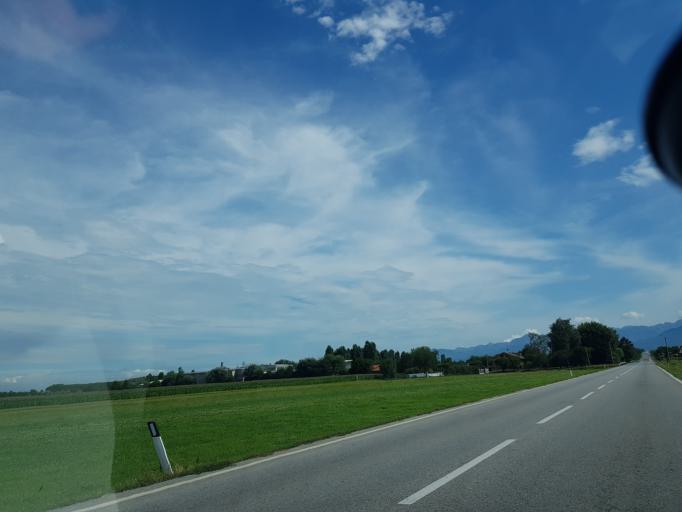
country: IT
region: Piedmont
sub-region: Provincia di Cuneo
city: Roata Rossi
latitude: 44.4601
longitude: 7.5189
